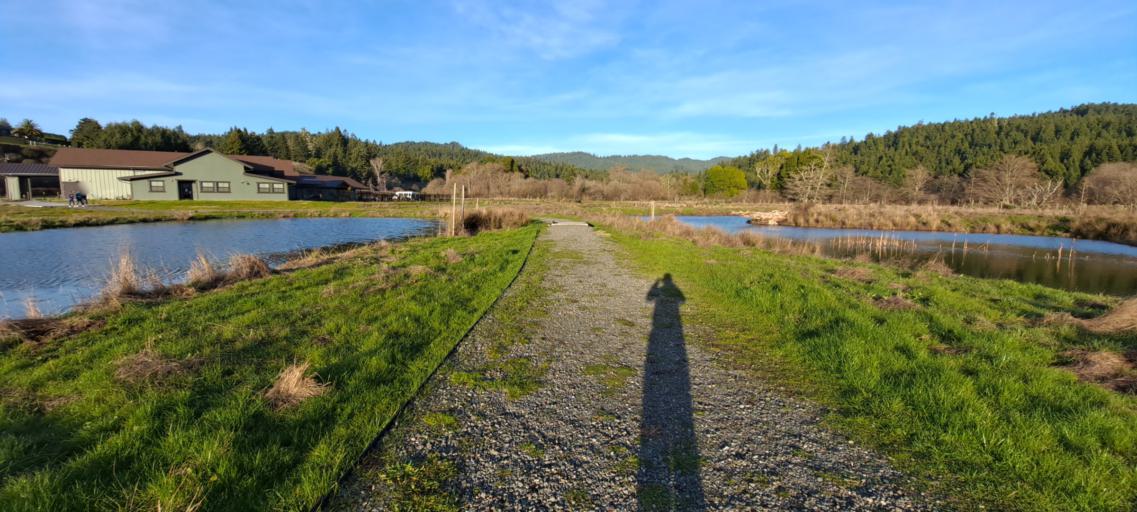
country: US
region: California
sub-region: Humboldt County
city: Fortuna
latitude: 40.5934
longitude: -124.1327
